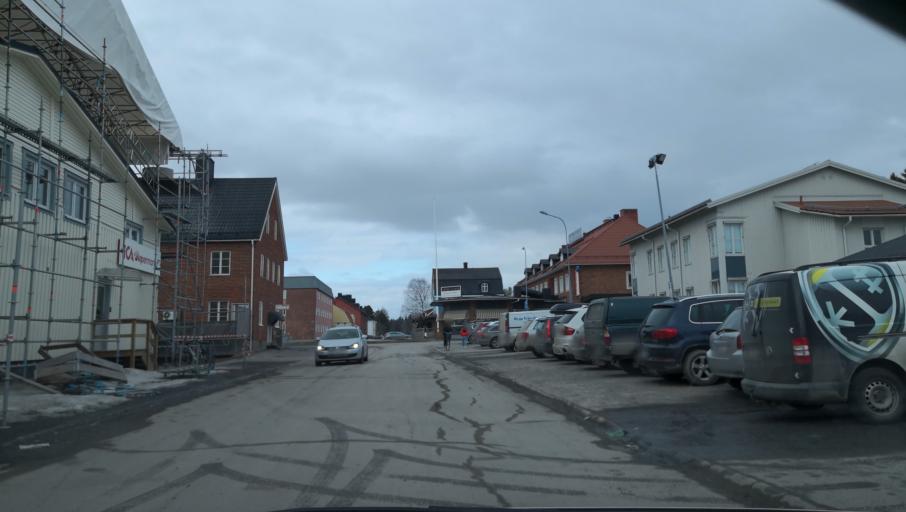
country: SE
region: Vaesterbotten
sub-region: Vannas Kommun
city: Vaennaes
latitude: 63.9080
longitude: 19.7534
